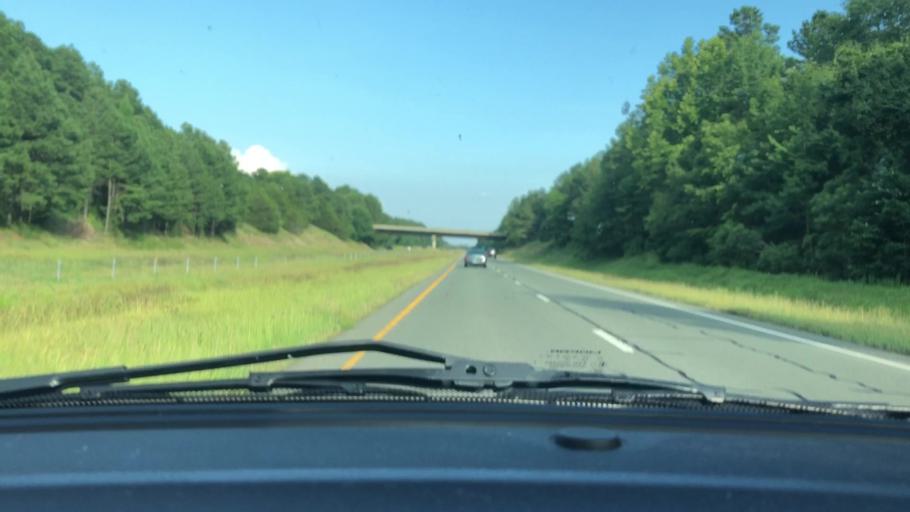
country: US
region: North Carolina
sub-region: Chatham County
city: Siler City
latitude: 35.7539
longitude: -79.4564
